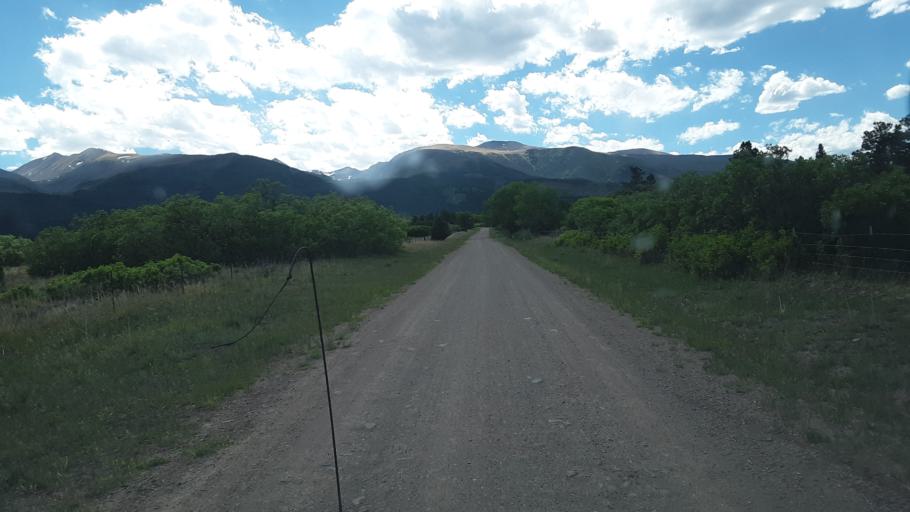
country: US
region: Colorado
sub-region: Custer County
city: Westcliffe
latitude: 38.2253
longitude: -105.6066
